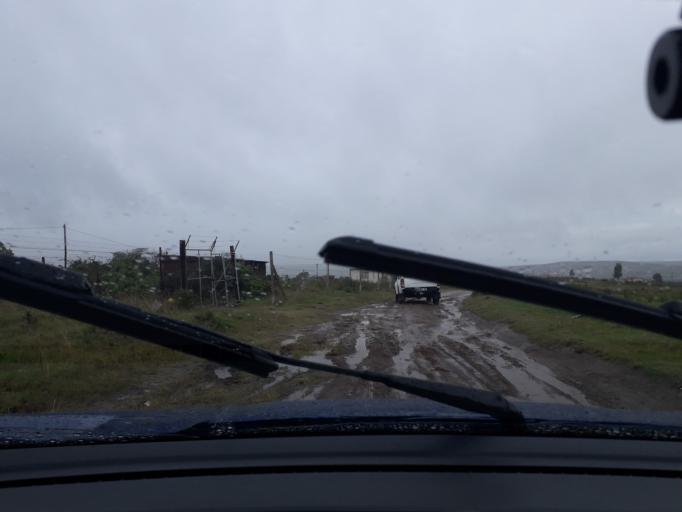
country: ZA
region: Eastern Cape
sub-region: Buffalo City Metropolitan Municipality
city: Bhisho
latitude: -32.8089
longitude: 27.3643
